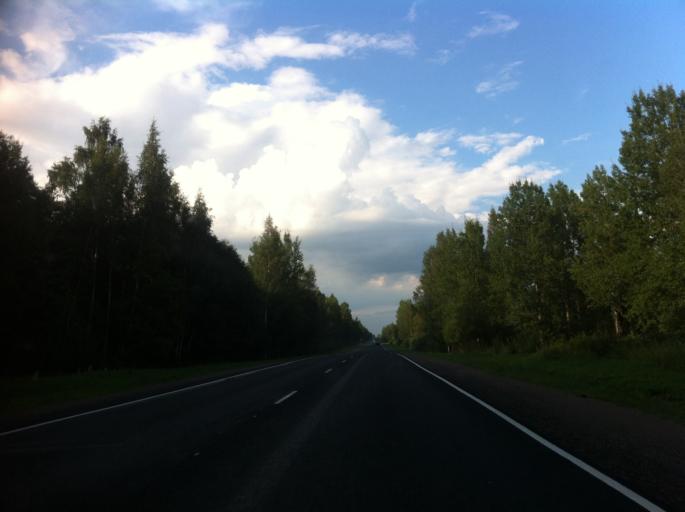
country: RU
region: Leningrad
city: Luga
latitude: 58.4967
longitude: 29.7851
